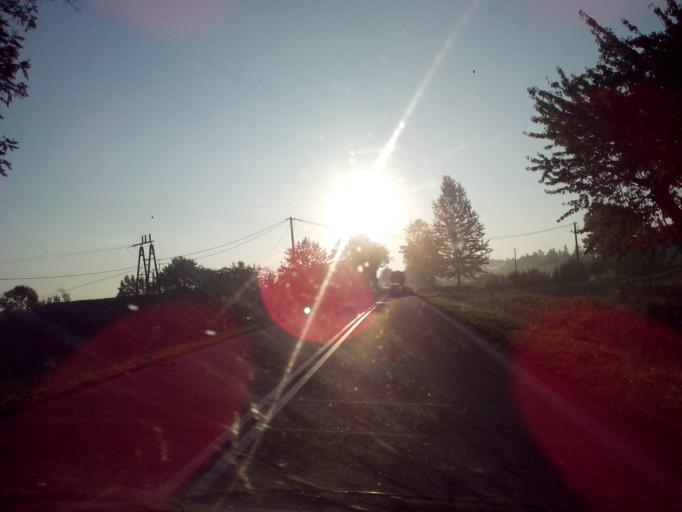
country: PL
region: Subcarpathian Voivodeship
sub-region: Powiat strzyzowski
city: Gwoznica Gorna
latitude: 49.8100
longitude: 22.0088
